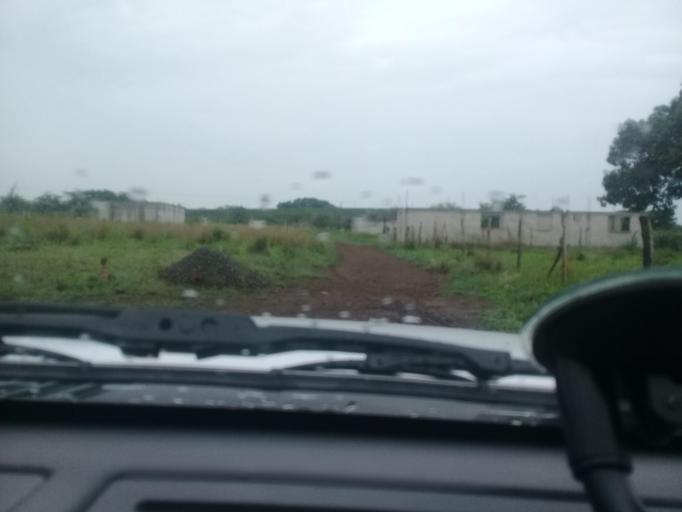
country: MX
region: Veracruz
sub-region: Puente Nacional
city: Cabezas
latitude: 19.3661
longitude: -96.3881
